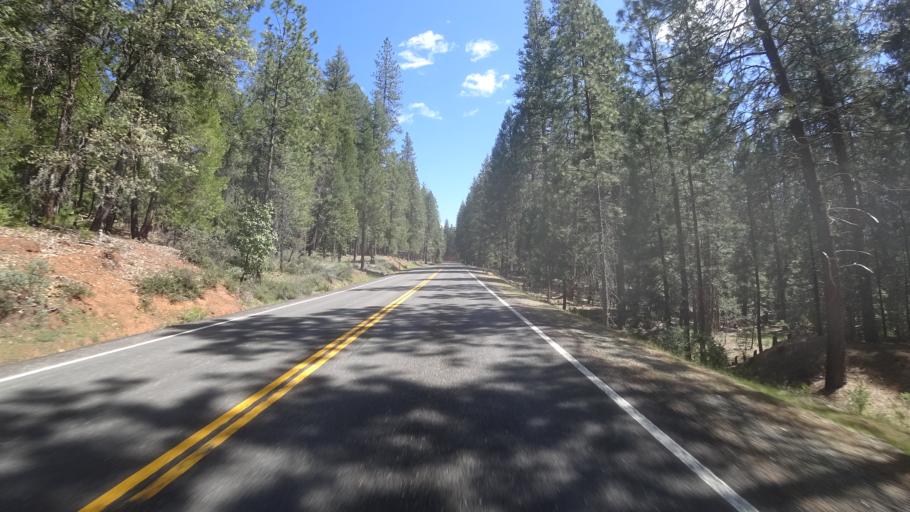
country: US
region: California
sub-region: Trinity County
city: Lewiston
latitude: 40.8488
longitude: -122.8485
